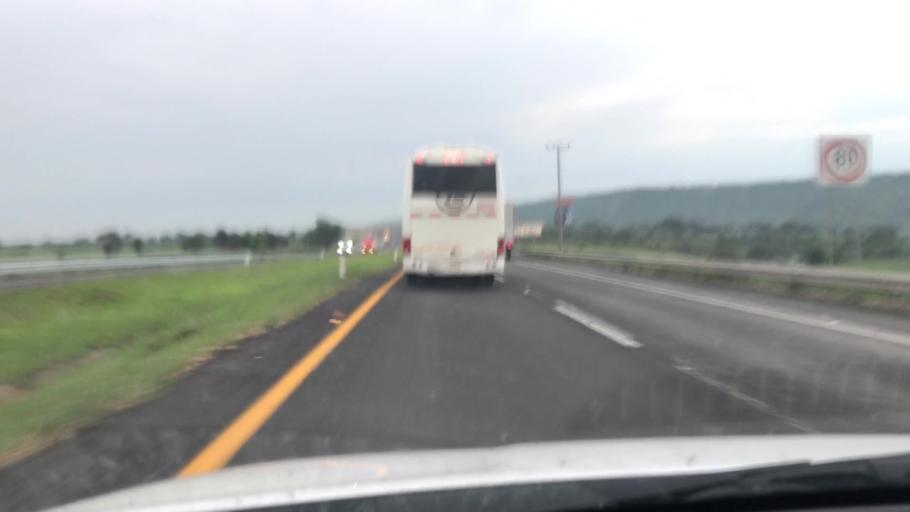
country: MX
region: Jalisco
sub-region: Zapotlanejo
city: La Mezquitera
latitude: 20.5437
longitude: -103.0274
